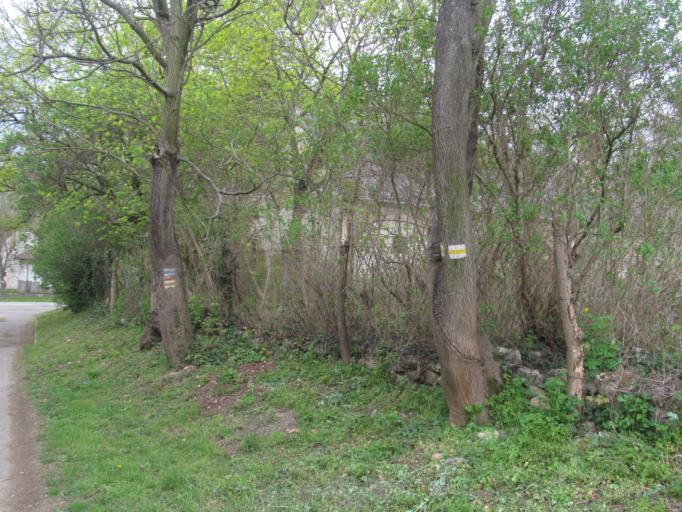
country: HU
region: Veszprem
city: Zanka
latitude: 46.9110
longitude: 17.6168
